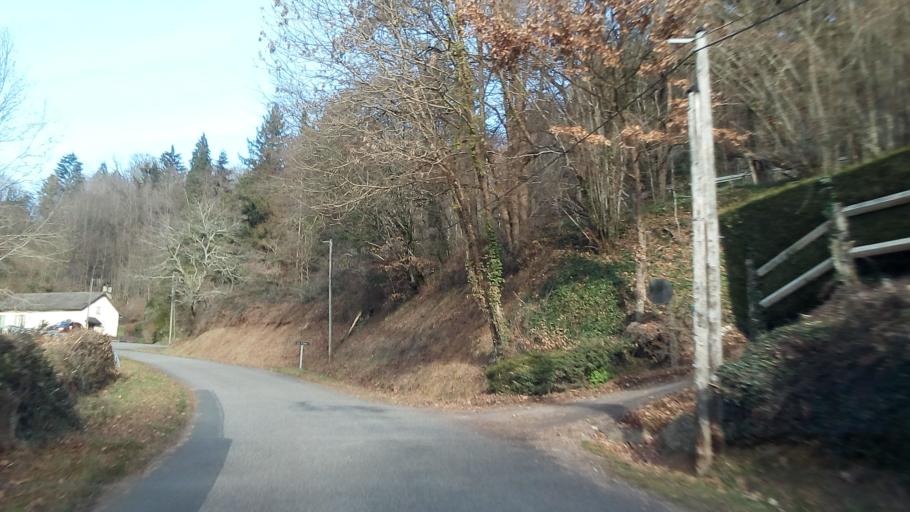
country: FR
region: Limousin
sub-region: Departement de la Correze
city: Naves
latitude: 45.3096
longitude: 1.7945
